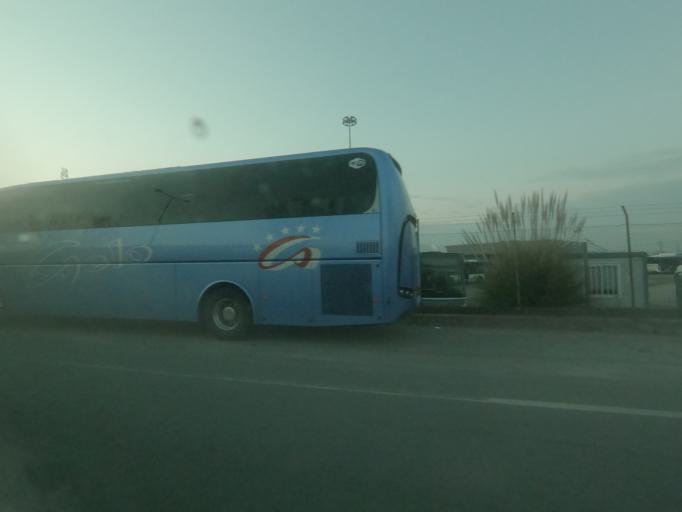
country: PT
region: Porto
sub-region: Matosinhos
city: Sao Mamede de Infesta
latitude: 41.1818
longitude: -8.6192
